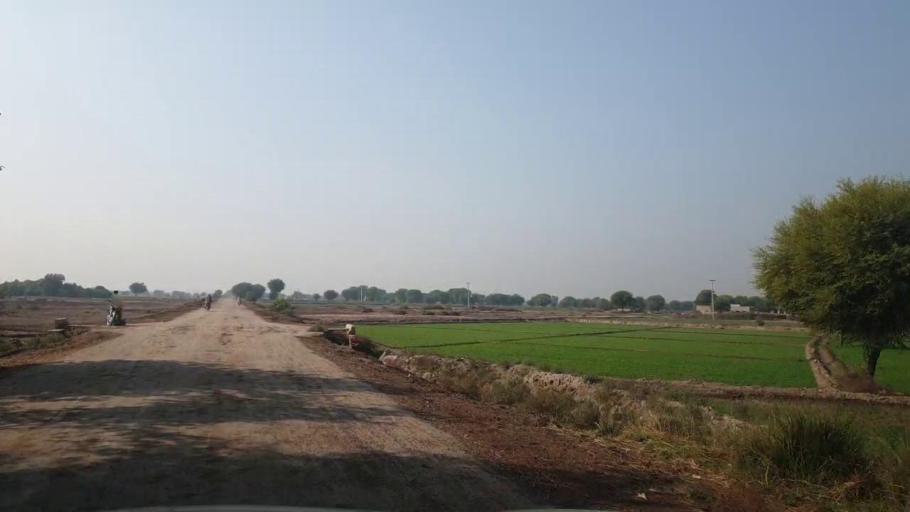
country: PK
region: Sindh
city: Bhan
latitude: 26.5169
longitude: 67.8020
